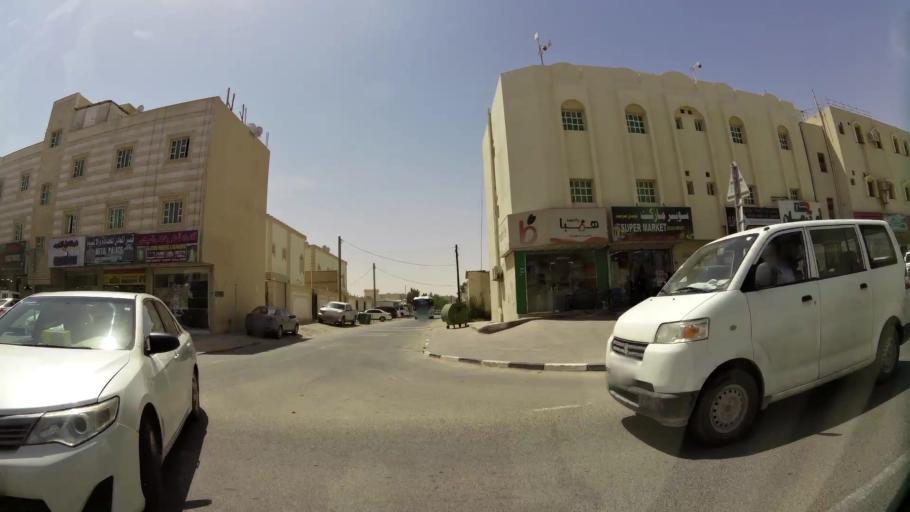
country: QA
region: Baladiyat ar Rayyan
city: Ar Rayyan
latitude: 25.2670
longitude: 51.4098
